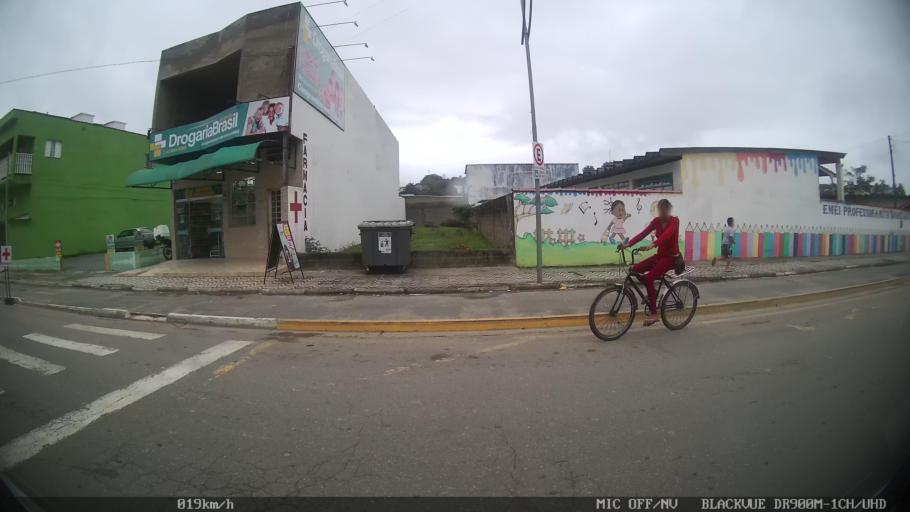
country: BR
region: Sao Paulo
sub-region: Juquia
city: Juquia
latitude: -24.3135
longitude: -47.6291
